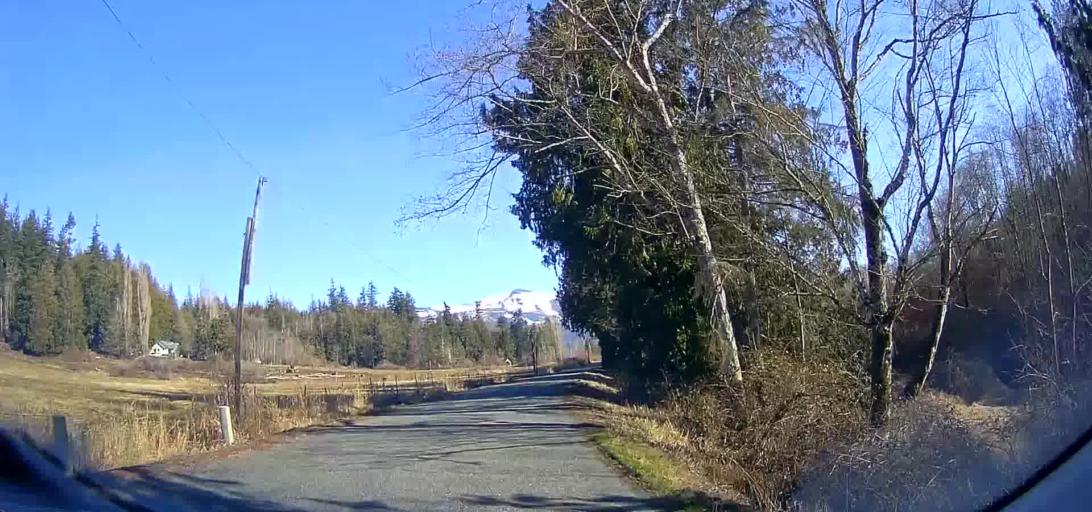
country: US
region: Washington
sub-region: Skagit County
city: Clear Lake
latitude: 48.4469
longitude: -122.2535
